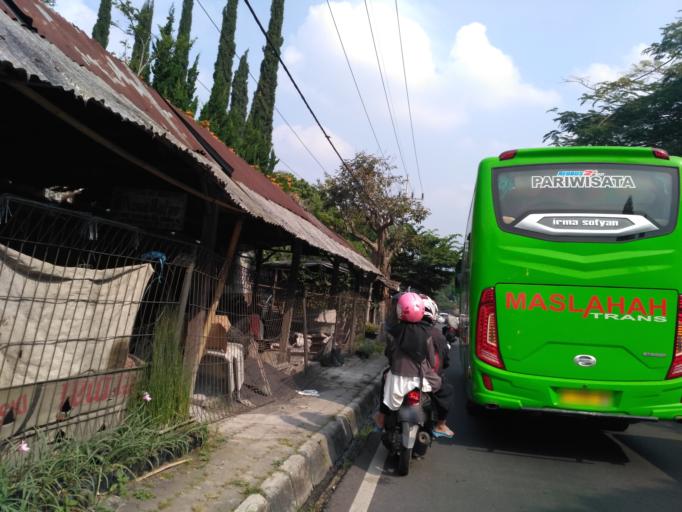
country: ID
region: East Java
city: Batu
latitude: -7.8557
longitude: 112.5271
